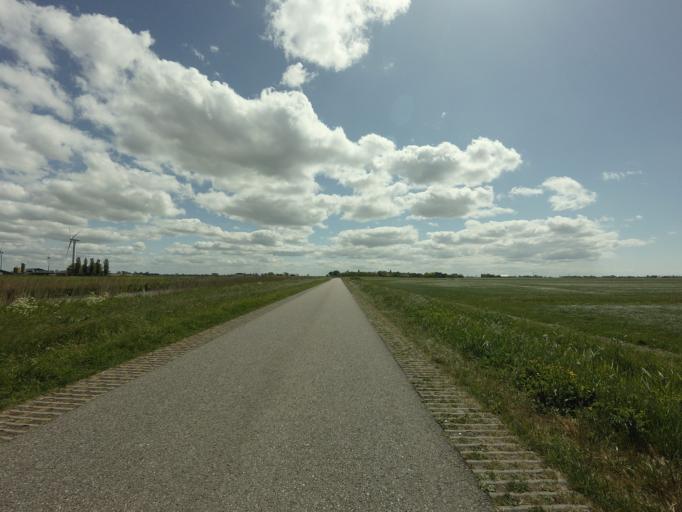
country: NL
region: Friesland
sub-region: Sudwest Fryslan
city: Makkum
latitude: 53.0907
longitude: 5.4156
